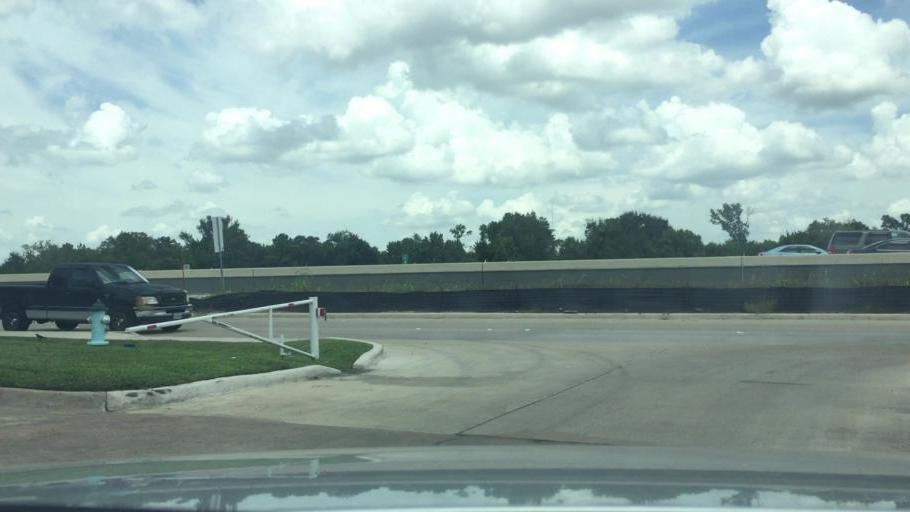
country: US
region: Texas
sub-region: Harris County
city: Jersey Village
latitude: 29.8631
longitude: -95.5267
